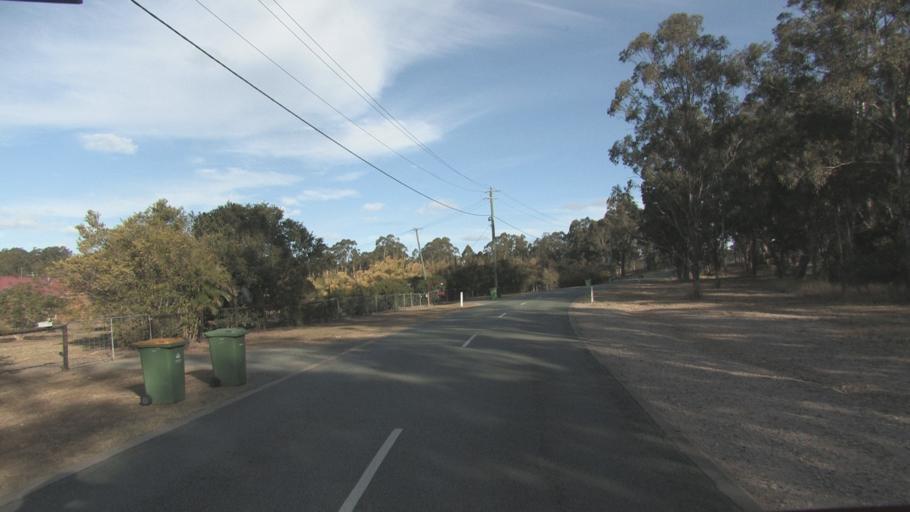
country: AU
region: Queensland
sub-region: Logan
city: Cedar Vale
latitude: -27.8809
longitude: 153.0105
